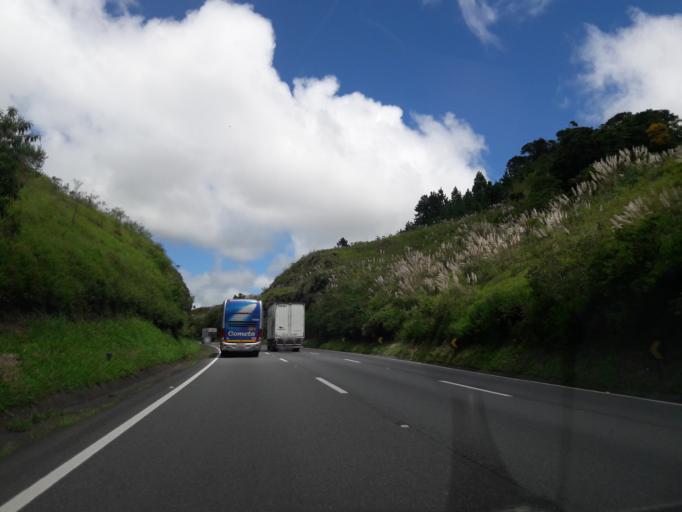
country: BR
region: Sao Paulo
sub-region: Cajati
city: Cajati
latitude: -24.9678
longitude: -48.4915
